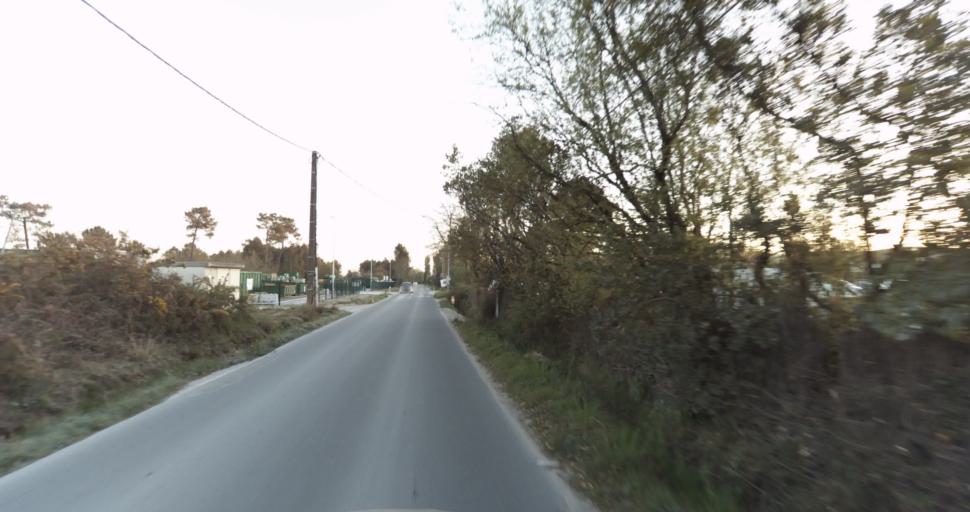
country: FR
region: Aquitaine
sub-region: Departement de la Gironde
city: Saint-Aubin-de-Medoc
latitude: 44.8072
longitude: -0.7274
